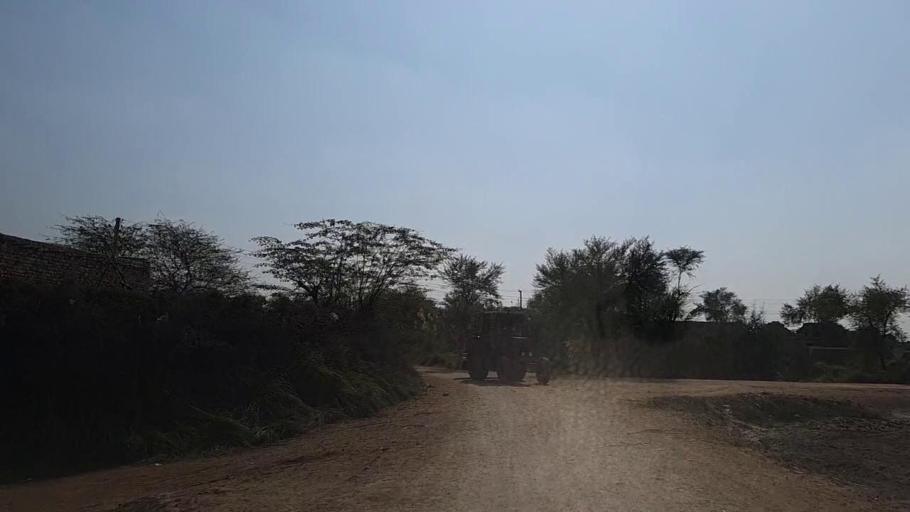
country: PK
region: Sindh
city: Daur
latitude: 26.4912
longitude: 68.2599
